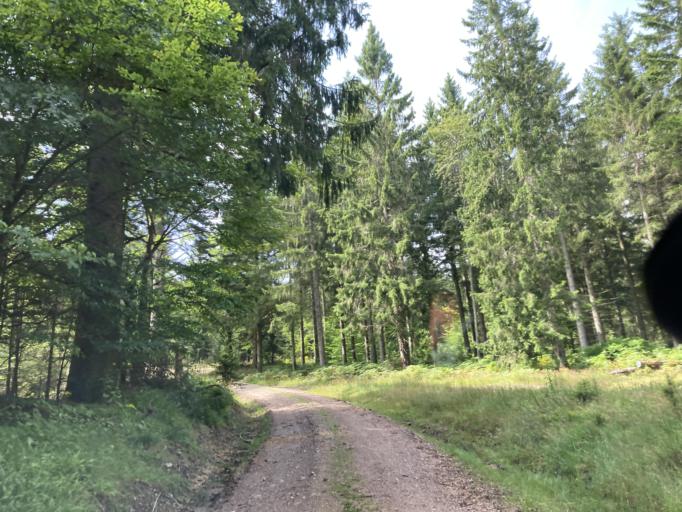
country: DE
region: Baden-Wuerttemberg
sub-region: Freiburg Region
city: Schonach im Schwarzwald
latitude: 48.1643
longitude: 8.1405
